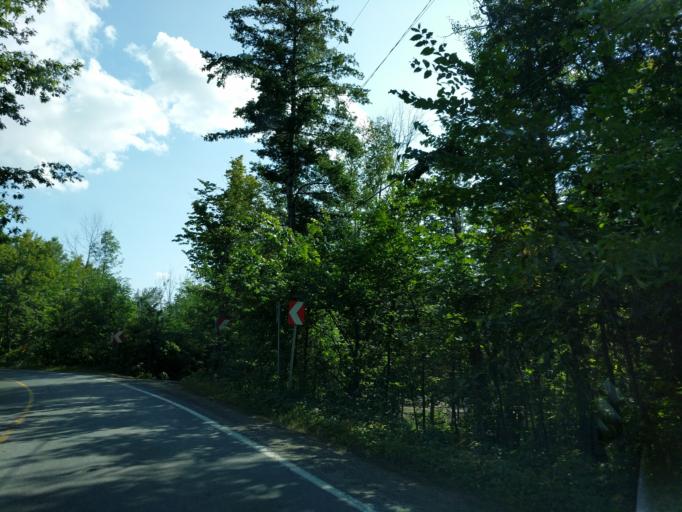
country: CA
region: Quebec
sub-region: Outaouais
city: Gatineau
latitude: 45.4814
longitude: -75.8631
